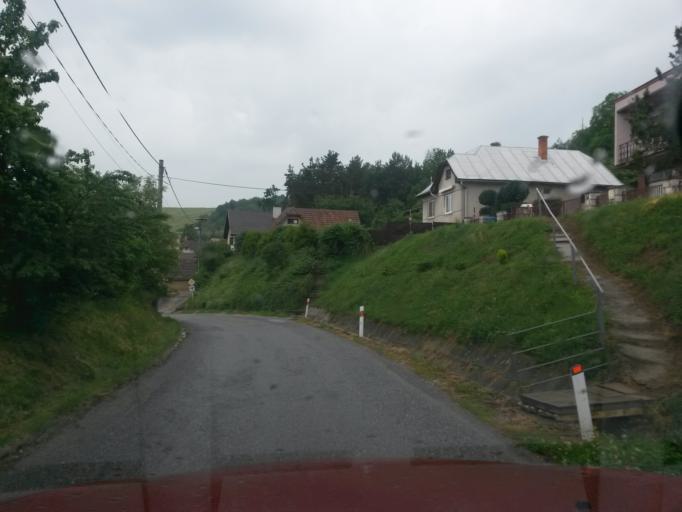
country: SK
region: Kosicky
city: Kosice
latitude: 48.7082
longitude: 21.1811
